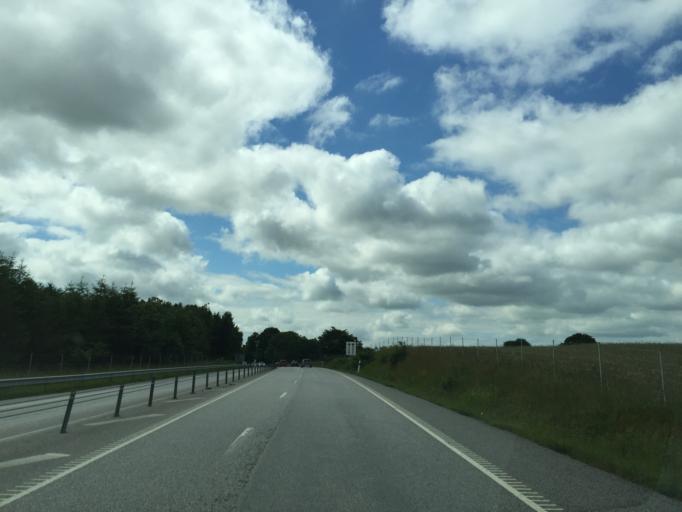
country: SE
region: Skane
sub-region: Svedala Kommun
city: Svedala
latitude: 55.5147
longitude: 13.2975
